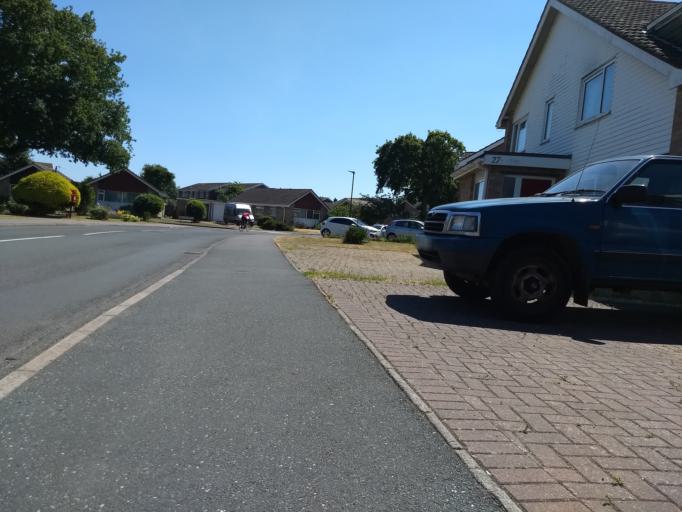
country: GB
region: England
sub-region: Isle of Wight
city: Gurnard
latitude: 50.7601
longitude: -1.3110
